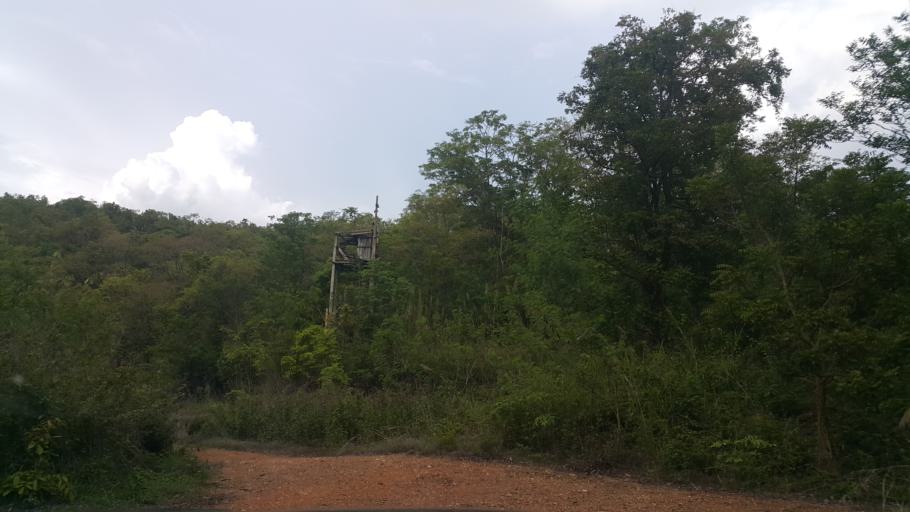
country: TH
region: Chiang Mai
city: Mae On
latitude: 18.7180
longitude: 99.2200
